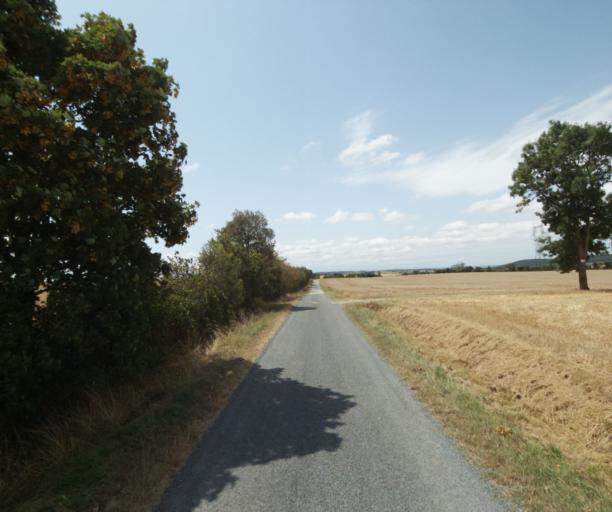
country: FR
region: Midi-Pyrenees
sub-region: Departement de la Haute-Garonne
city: Saint-Felix-Lauragais
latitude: 43.4323
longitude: 1.8820
